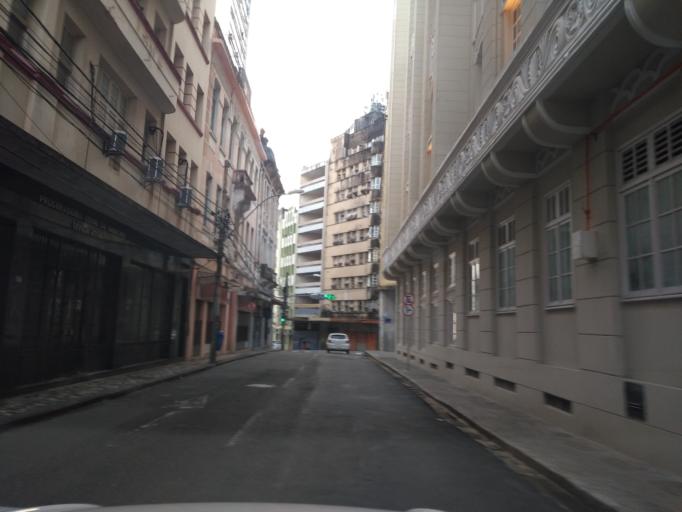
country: BR
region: Bahia
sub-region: Salvador
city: Salvador
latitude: -12.9762
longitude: -38.5134
